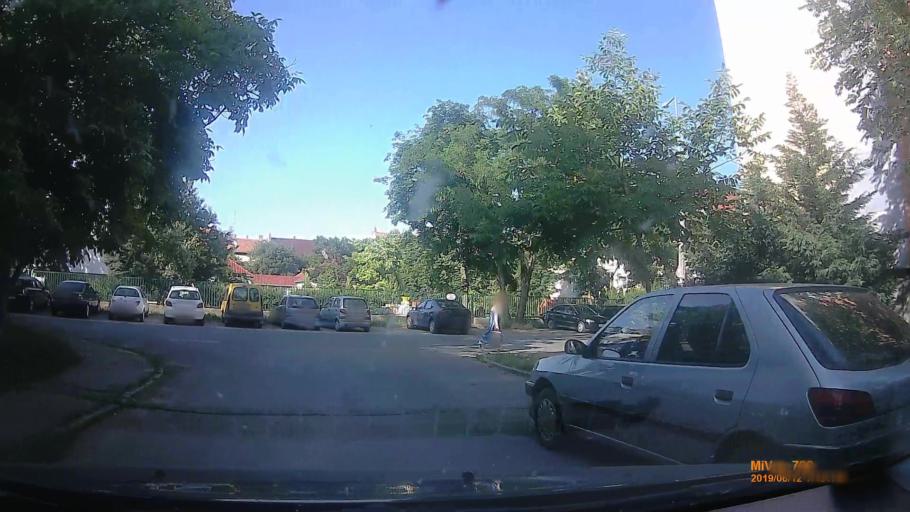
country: HU
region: Csongrad
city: Szeged
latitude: 46.2623
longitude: 20.1647
